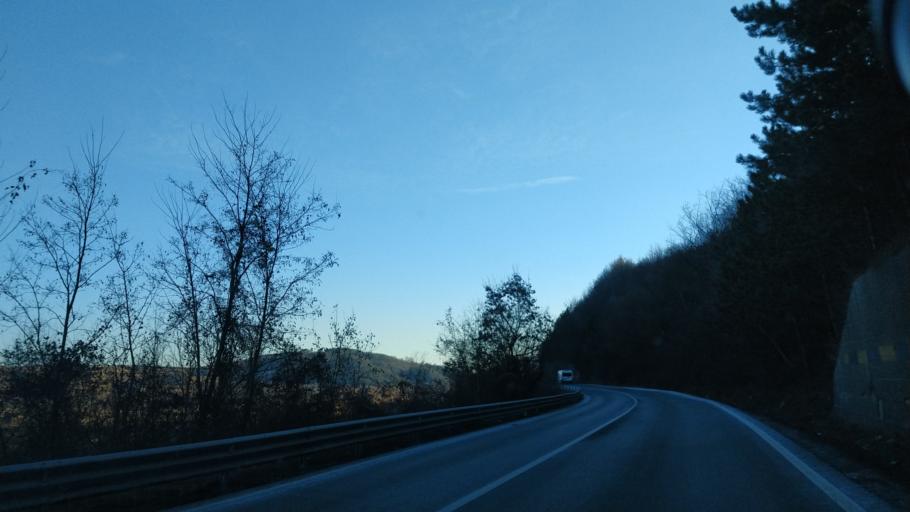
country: RO
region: Bacau
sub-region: Comuna Helegiu
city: Bratila
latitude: 46.3073
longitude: 26.7507
